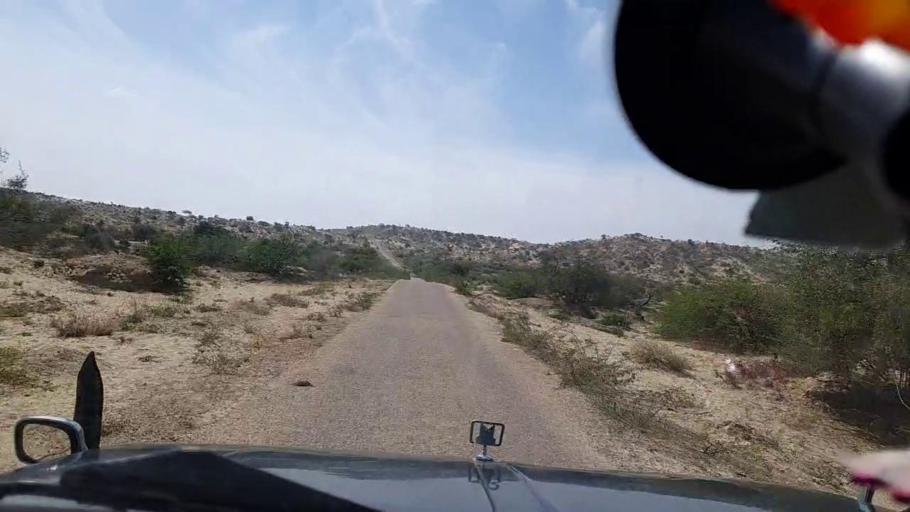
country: PK
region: Sindh
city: Diplo
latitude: 24.3675
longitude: 69.5840
